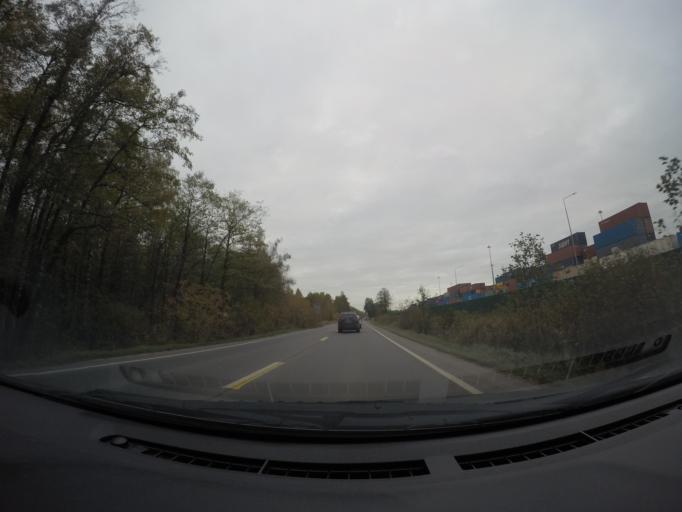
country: RU
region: Moskovskaya
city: Elektrougli
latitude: 55.7252
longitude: 38.2414
